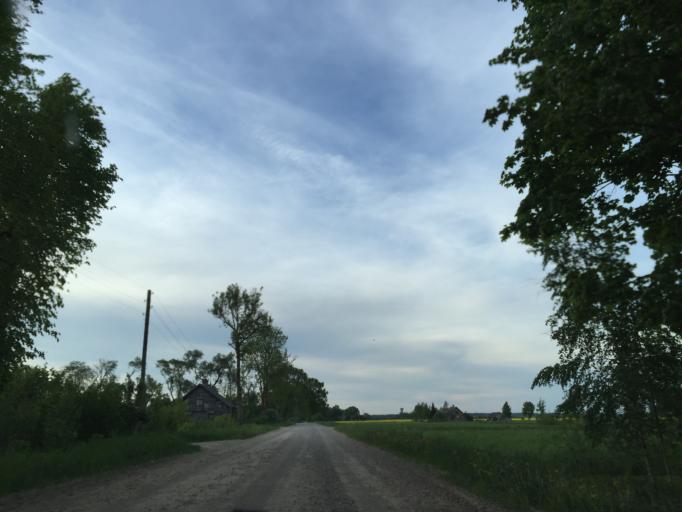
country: LV
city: Tireli
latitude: 56.7060
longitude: 23.4980
